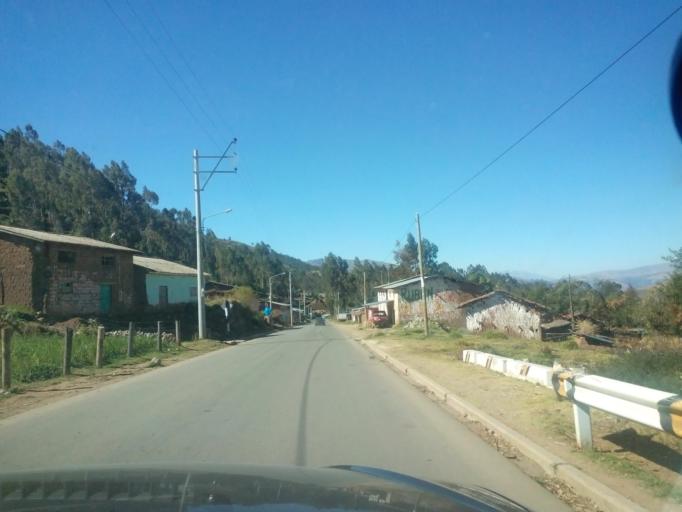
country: PE
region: Apurimac
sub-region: Provincia de Andahuaylas
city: Talavera
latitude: -13.6508
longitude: -73.5204
